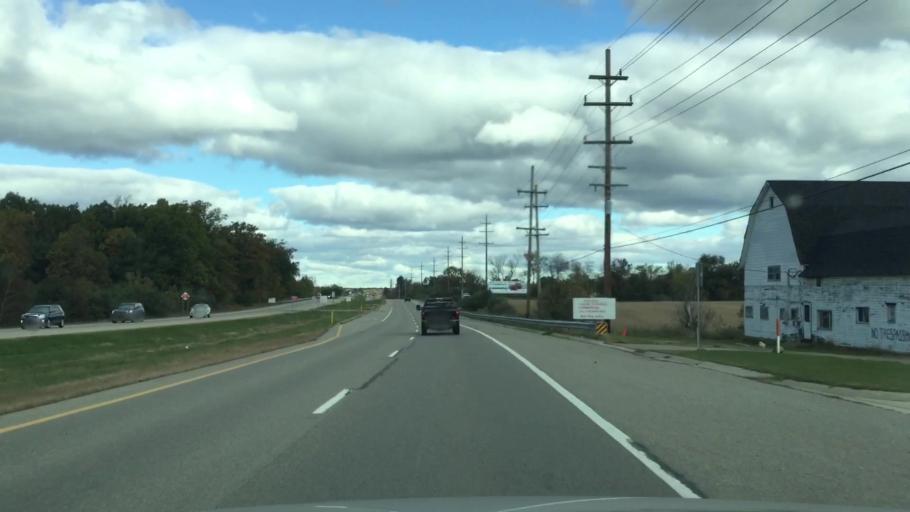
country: US
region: Michigan
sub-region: Lapeer County
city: Lapeer
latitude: 42.9597
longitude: -83.3139
